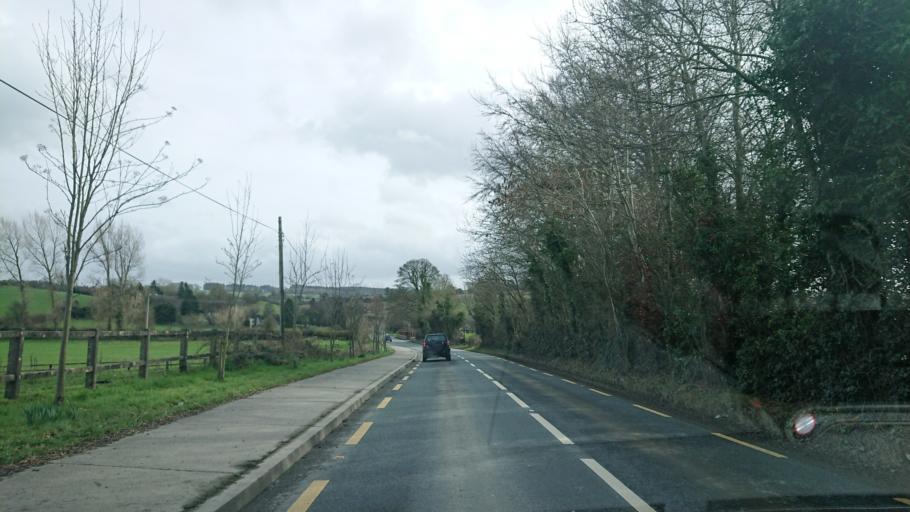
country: IE
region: Leinster
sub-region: Kildare
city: Eadestown
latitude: 53.2001
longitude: -6.5735
